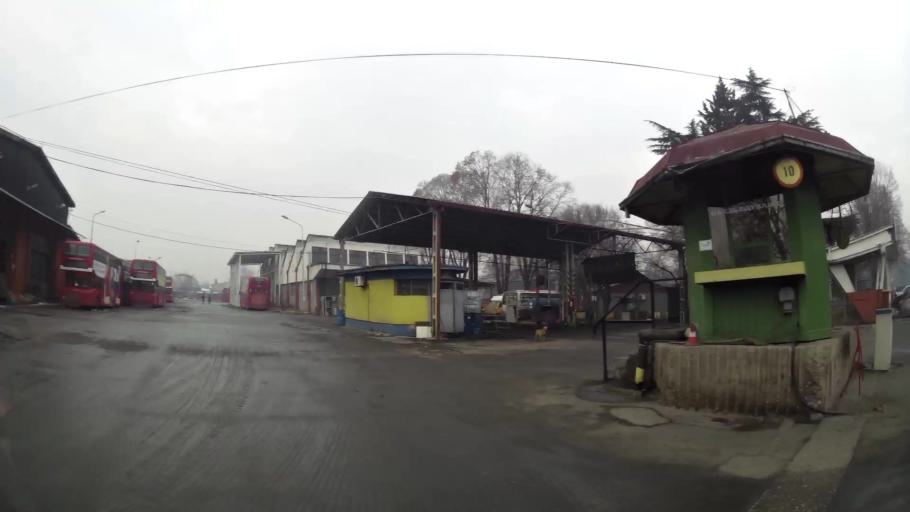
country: MK
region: Cair
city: Cair
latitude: 42.0003
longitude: 21.4652
